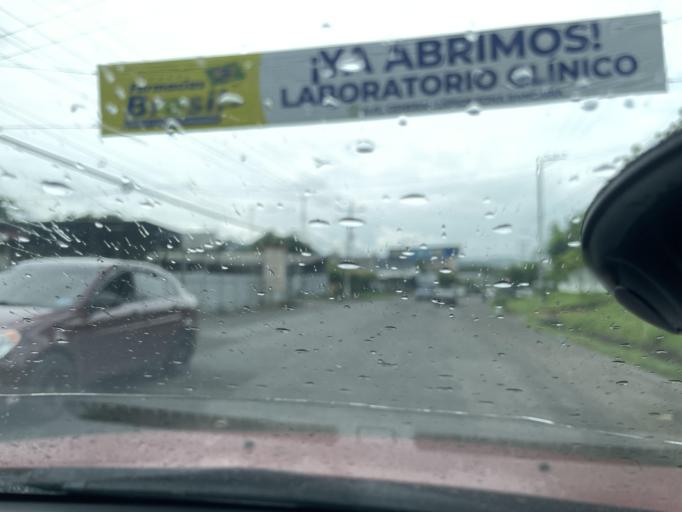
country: SV
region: La Union
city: Santa Rosa de Lima
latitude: 13.6210
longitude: -87.8977
